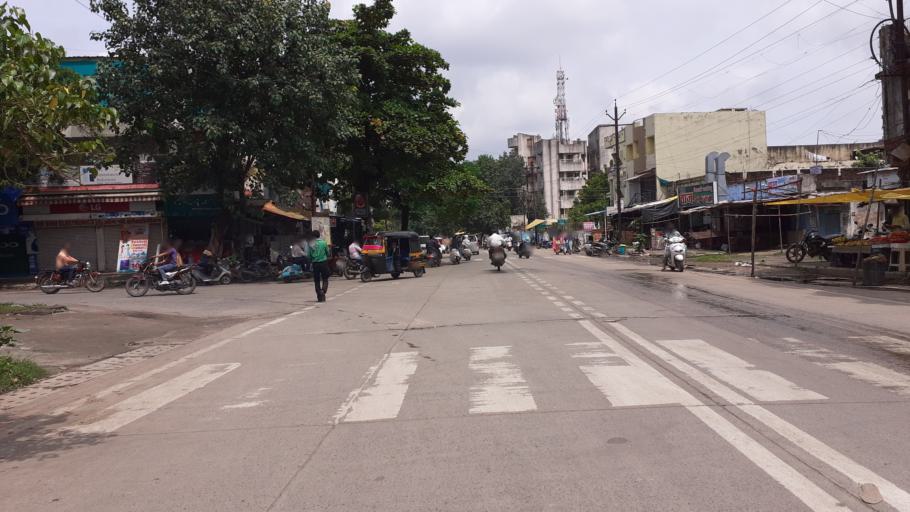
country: IN
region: Maharashtra
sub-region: Nagpur Division
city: Nagpur
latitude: 21.1170
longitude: 79.1110
